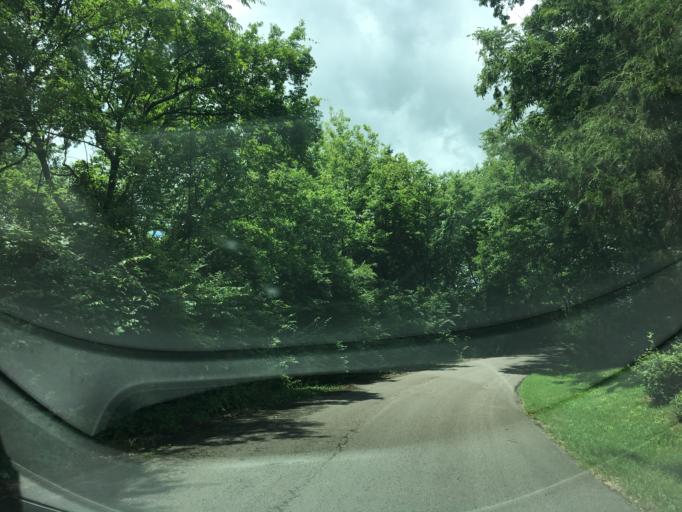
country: US
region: Tennessee
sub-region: Davidson County
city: Forest Hills
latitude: 36.0840
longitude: -86.8447
